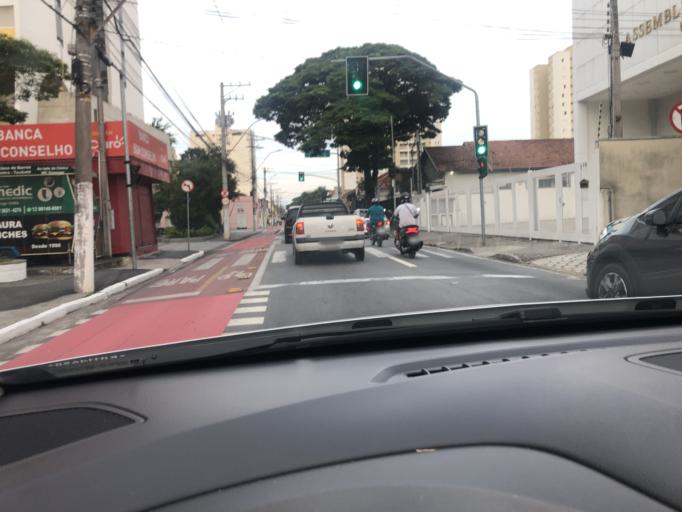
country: BR
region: Sao Paulo
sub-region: Taubate
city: Taubate
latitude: -23.0323
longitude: -45.5653
